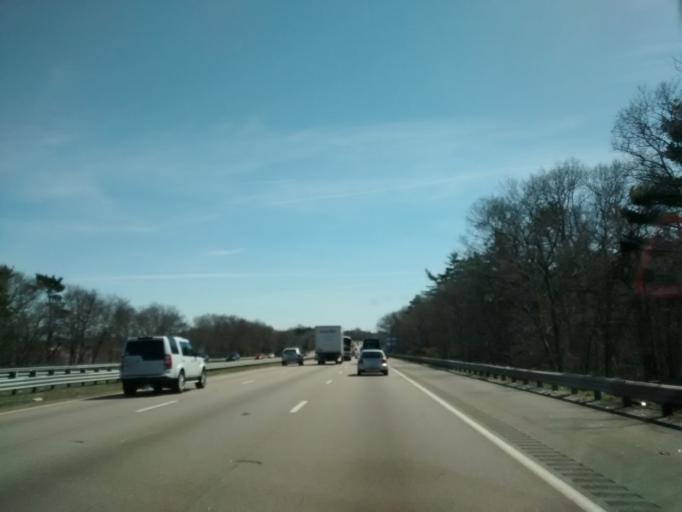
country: US
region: Massachusetts
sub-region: Norfolk County
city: Randolph
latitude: 42.1841
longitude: -71.0765
